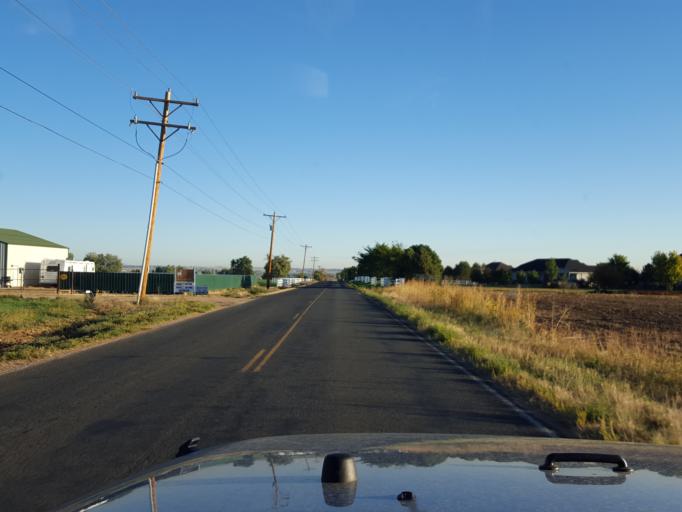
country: US
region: Colorado
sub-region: Weld County
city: Frederick
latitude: 40.1053
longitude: -104.9988
